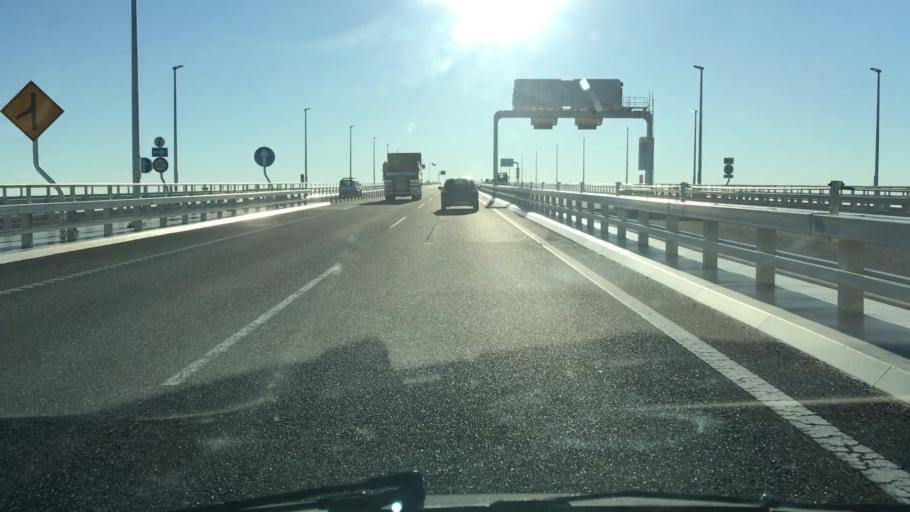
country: JP
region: Chiba
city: Kisarazu
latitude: 35.4609
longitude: 139.8796
